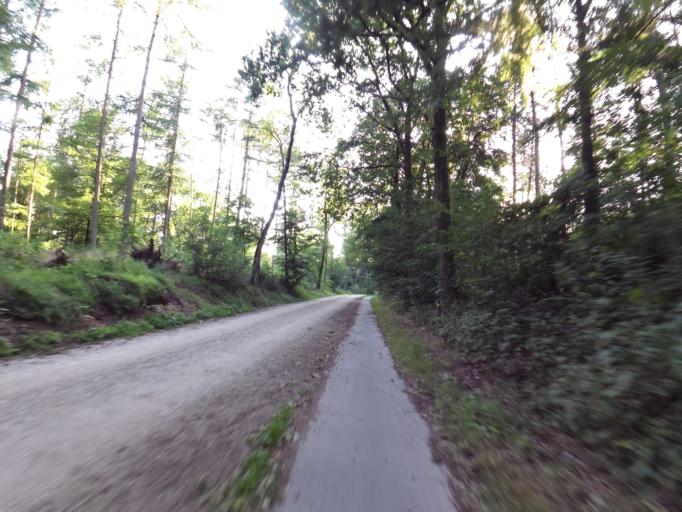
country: NL
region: Gelderland
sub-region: Gemeente Doetinchem
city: Doetinchem
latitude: 51.9998
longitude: 6.2587
